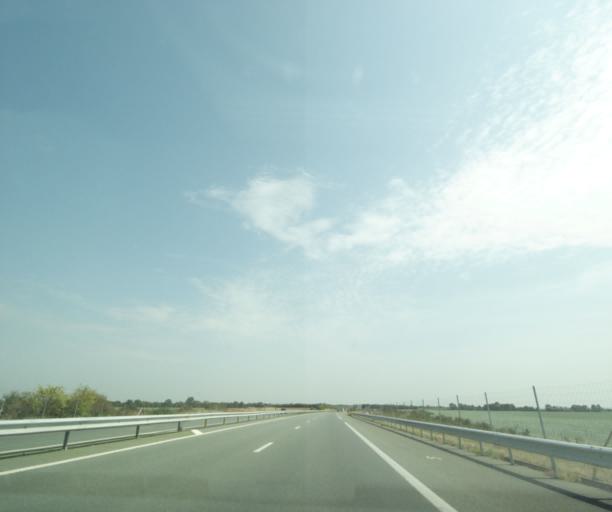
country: FR
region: Poitou-Charentes
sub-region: Departement des Deux-Sevres
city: Echire
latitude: 46.4211
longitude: -0.4269
